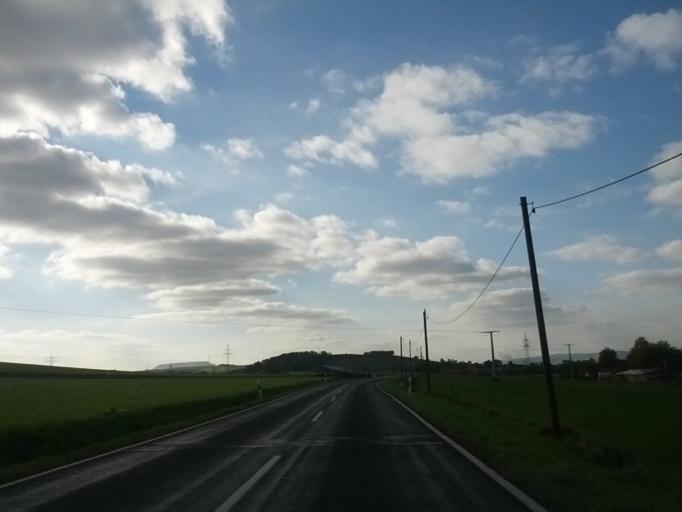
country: DE
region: Thuringia
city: Frauensee
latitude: 50.9394
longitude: 10.1208
